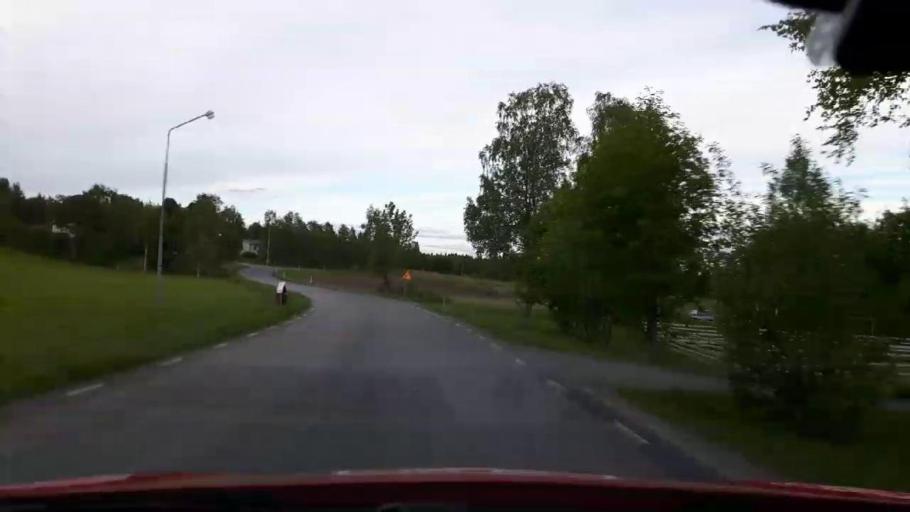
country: SE
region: Jaemtland
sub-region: Bergs Kommun
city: Hoverberg
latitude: 63.0300
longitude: 14.4715
